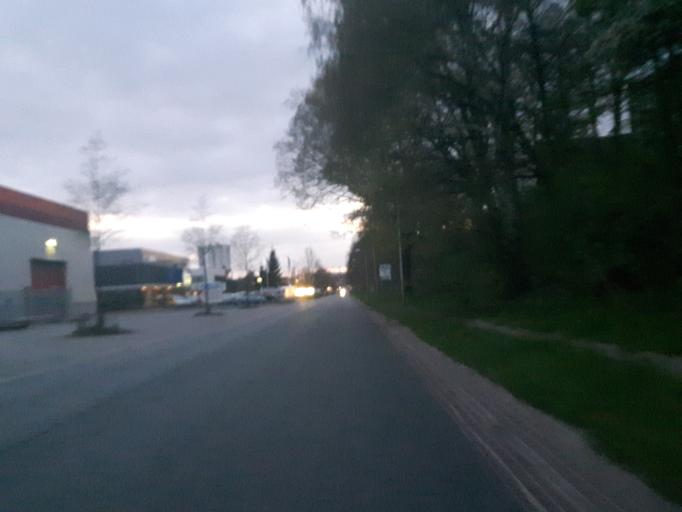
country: NL
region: Overijssel
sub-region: Gemeente Enschede
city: Enschede
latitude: 52.2279
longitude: 6.8510
